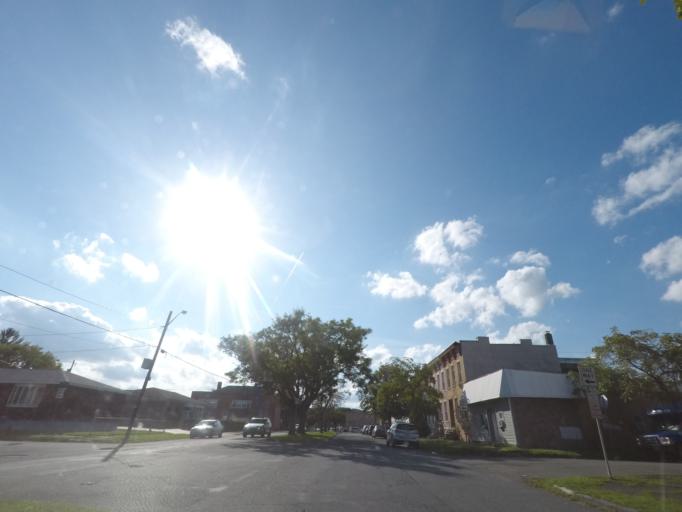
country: US
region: New York
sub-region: Albany County
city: Watervliet
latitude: 42.7329
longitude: -73.7021
